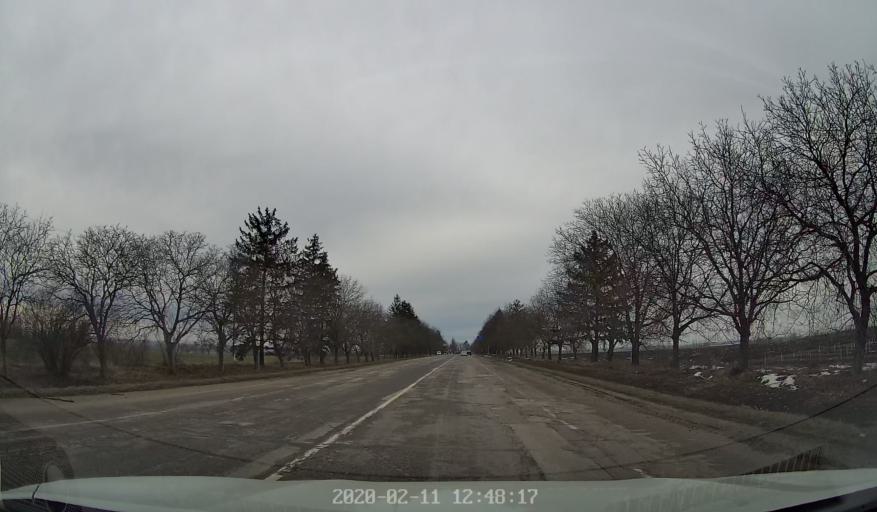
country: MD
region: Briceni
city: Briceni
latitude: 48.2796
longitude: 27.1498
